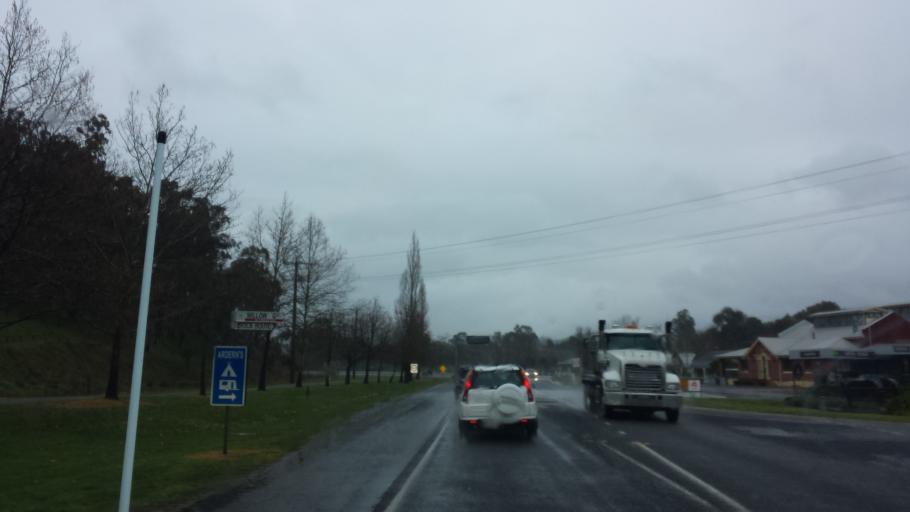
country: AU
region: Victoria
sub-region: Wangaratta
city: Wangaratta
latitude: -36.5679
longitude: 146.7304
